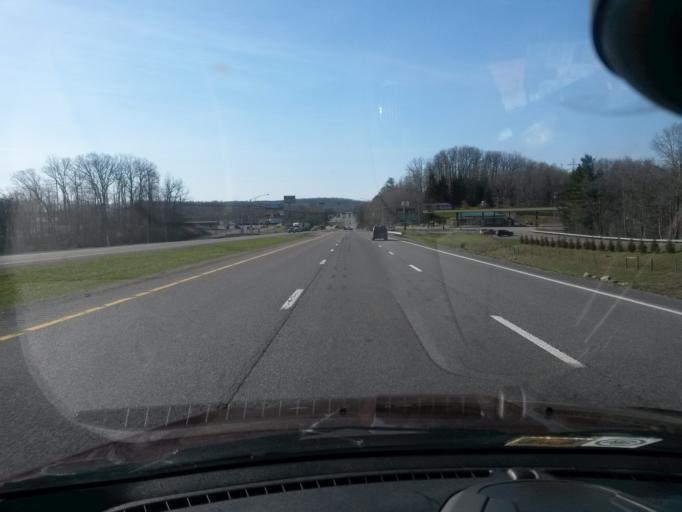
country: US
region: West Virginia
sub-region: Raleigh County
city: Bradley
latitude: 37.8764
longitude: -81.1905
